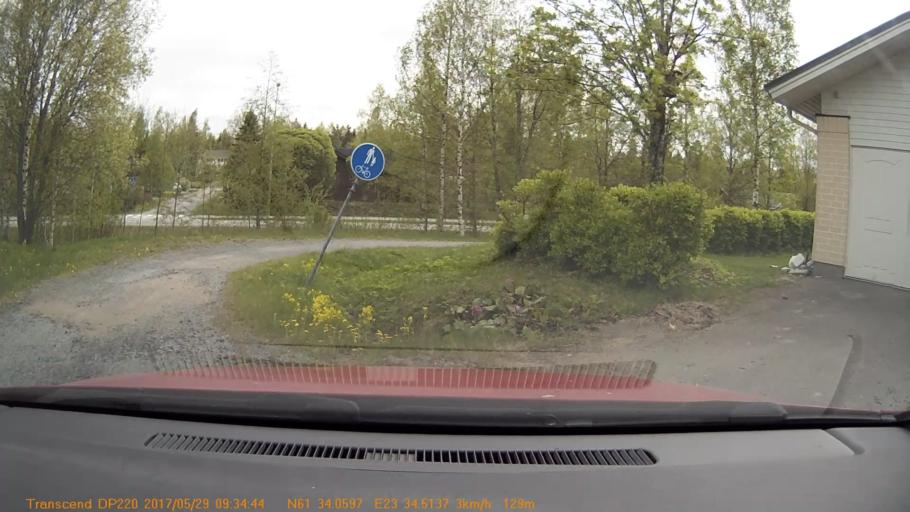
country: FI
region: Pirkanmaa
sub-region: Tampere
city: Yloejaervi
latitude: 61.5677
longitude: 23.5751
